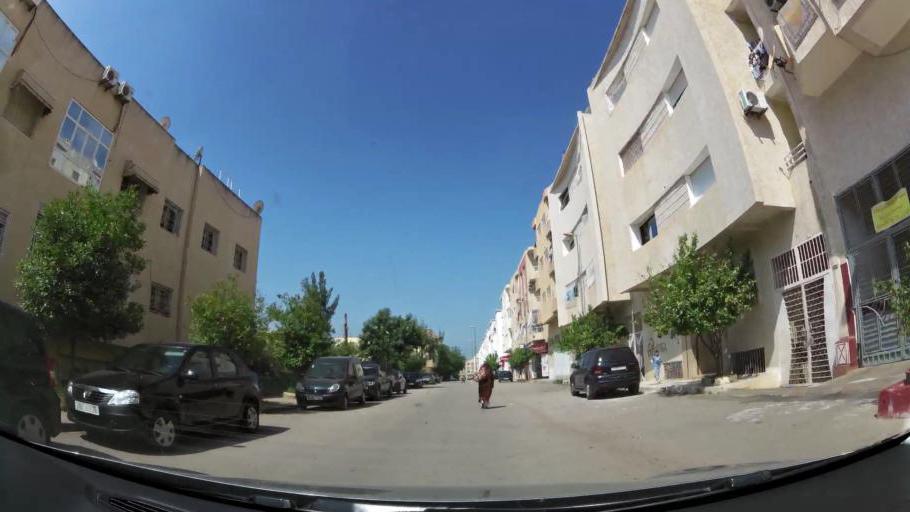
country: MA
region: Fes-Boulemane
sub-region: Fes
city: Fes
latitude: 34.0596
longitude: -5.0222
